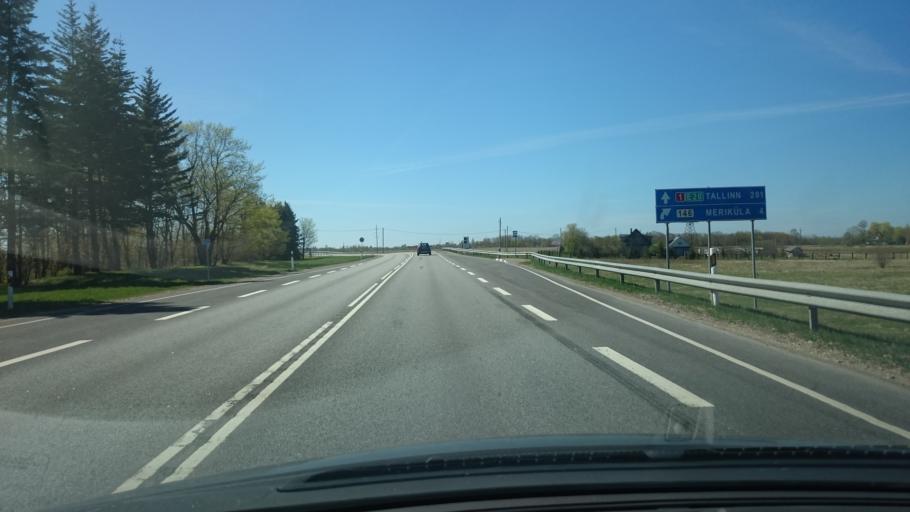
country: EE
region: Ida-Virumaa
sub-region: Narva-Joesuu linn
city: Narva-Joesuu
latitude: 59.4068
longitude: 28.0338
